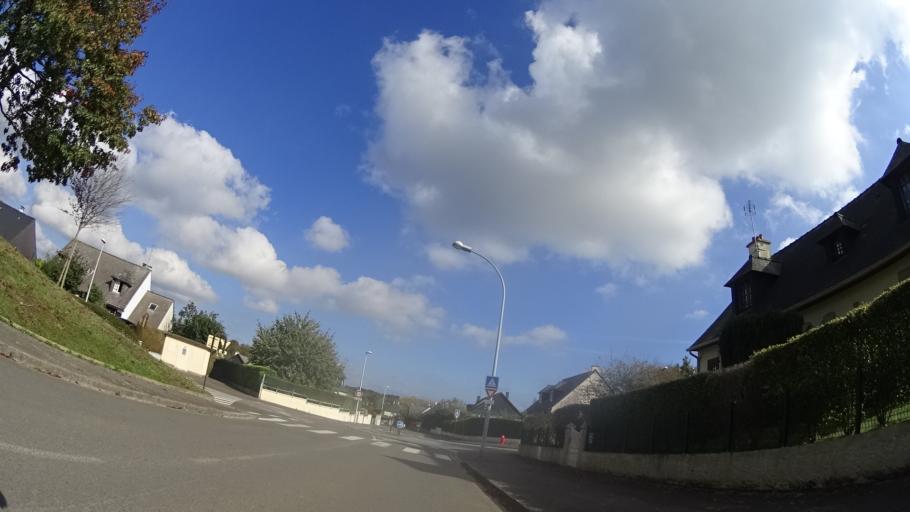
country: FR
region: Brittany
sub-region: Departement d'Ille-et-Vilaine
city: Geveze
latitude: 48.2183
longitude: -1.7885
